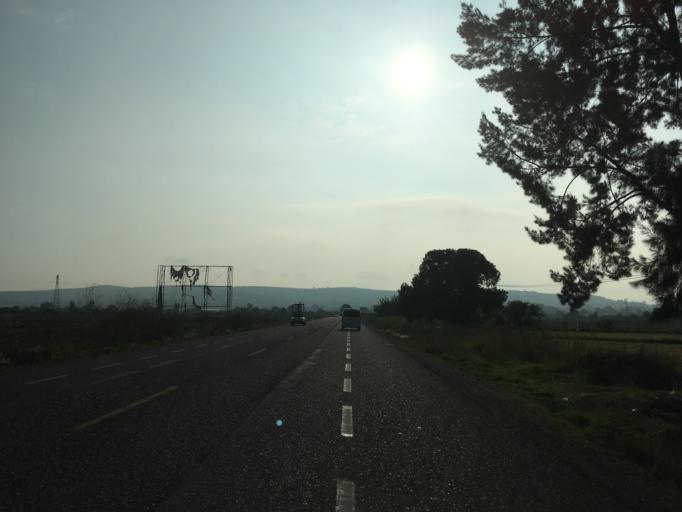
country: MX
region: Oaxaca
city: San Andres Sinaxtla
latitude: 17.4661
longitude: -97.2753
